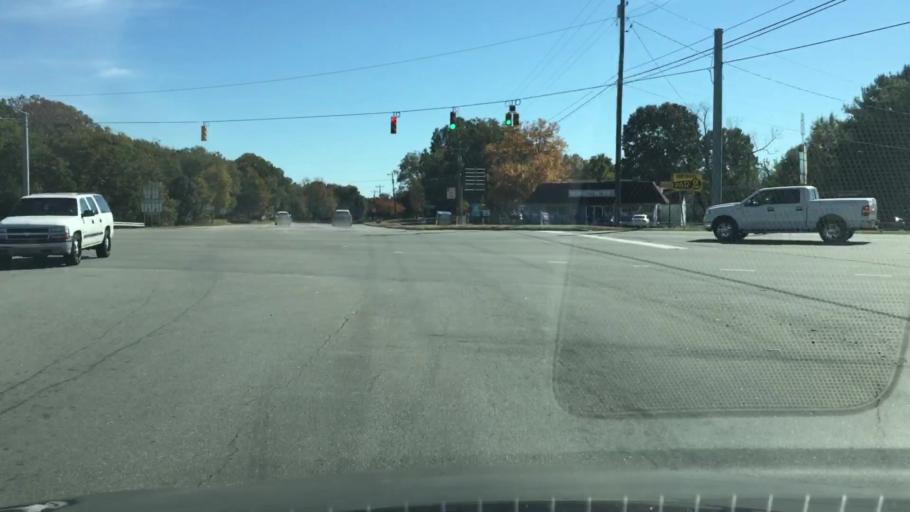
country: US
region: North Carolina
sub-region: Rockingham County
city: Reidsville
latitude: 36.3150
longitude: -79.6721
